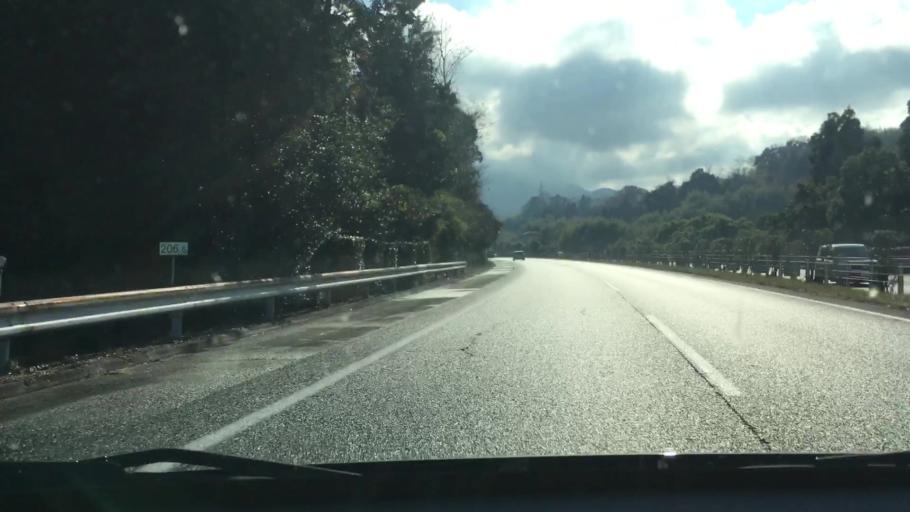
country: JP
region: Kumamoto
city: Matsubase
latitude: 32.5592
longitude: 130.6964
